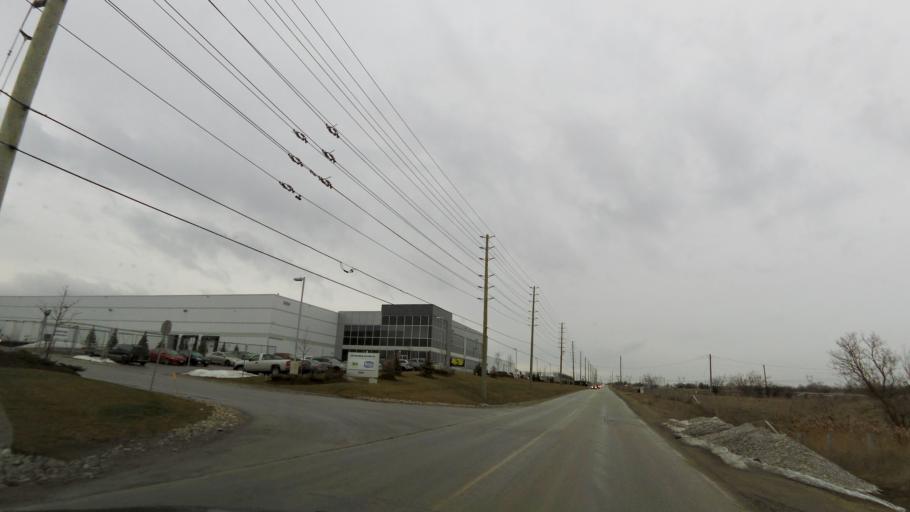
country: CA
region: Ontario
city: Vaughan
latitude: 43.7977
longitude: -79.6537
